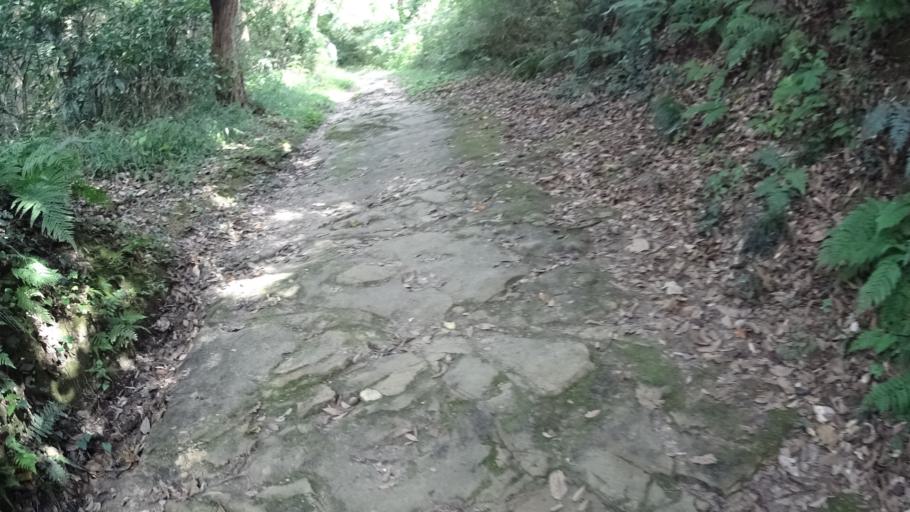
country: JP
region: Kanagawa
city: Zushi
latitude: 35.3015
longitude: 139.6031
